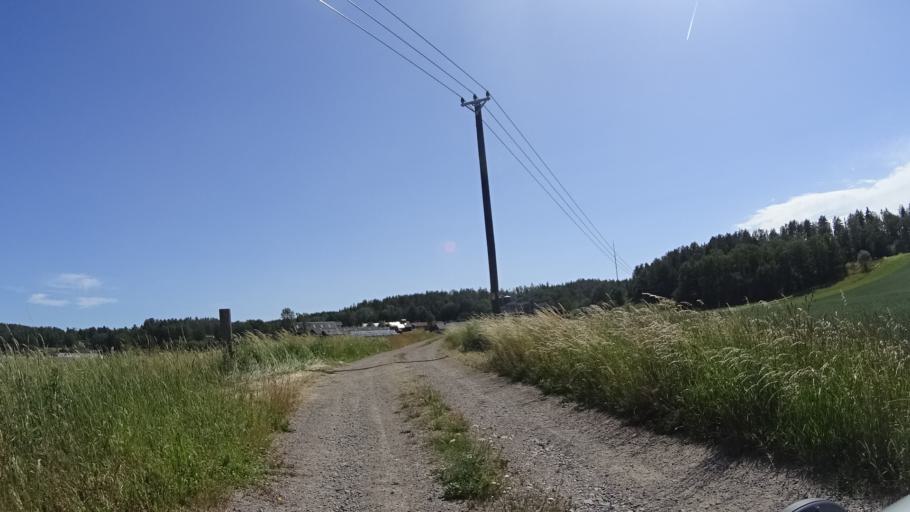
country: SE
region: Kalmar
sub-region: Vasterviks Kommun
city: Gamleby
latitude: 57.9167
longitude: 16.4060
